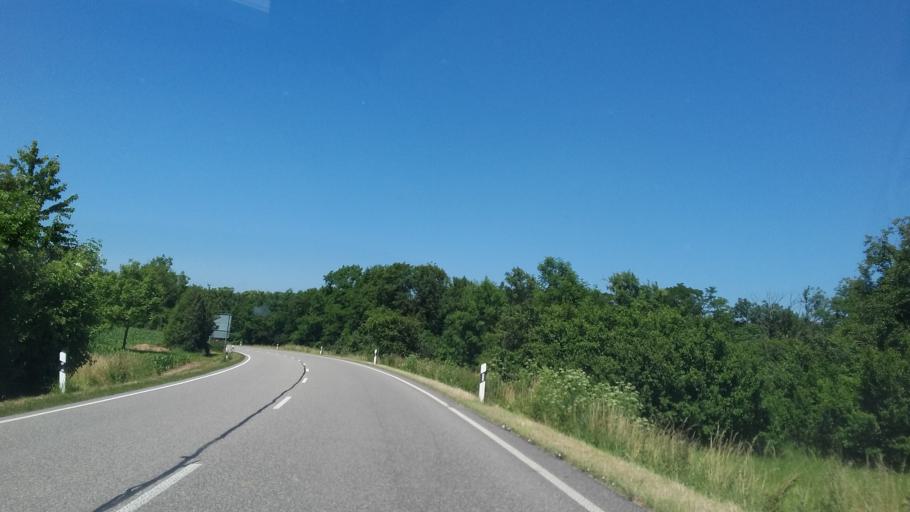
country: DE
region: Baden-Wuerttemberg
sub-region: Regierungsbezirk Stuttgart
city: Vaihingen an der Enz
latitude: 48.9311
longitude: 8.9491
